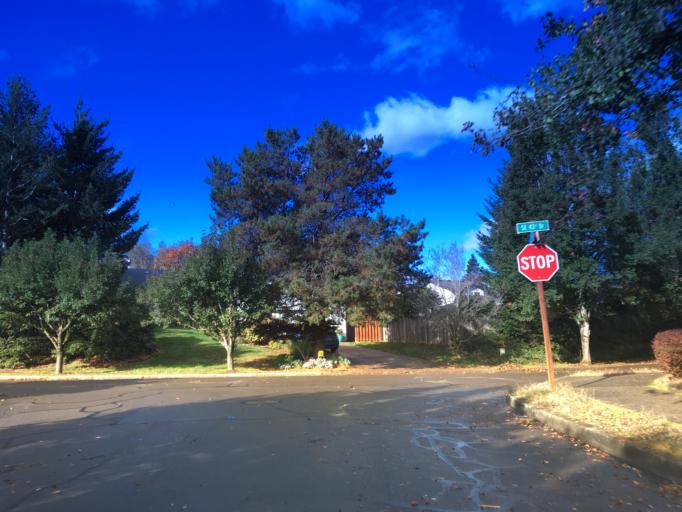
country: US
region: Oregon
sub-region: Multnomah County
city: Troutdale
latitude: 45.5108
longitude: -122.3819
